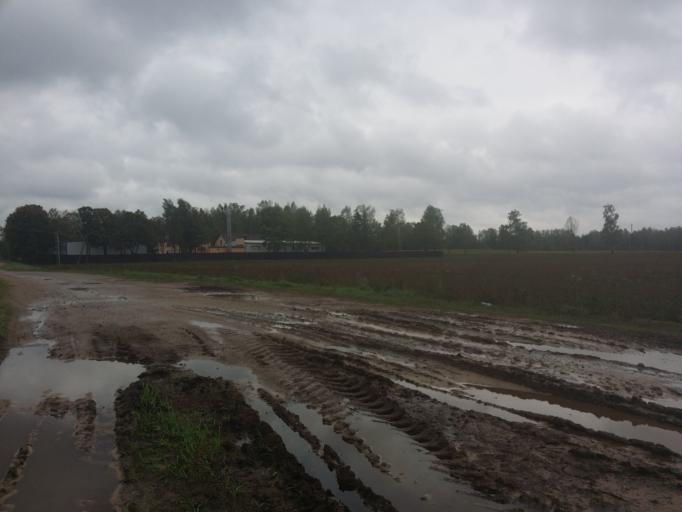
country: BY
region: Minsk
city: Chervyen'
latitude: 53.7651
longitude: 28.2518
